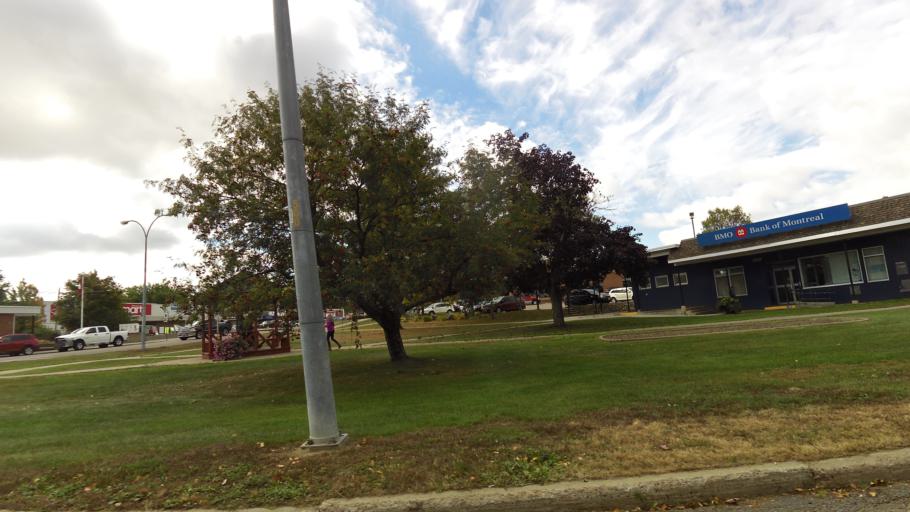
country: CA
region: Ontario
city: Deep River
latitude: 46.1016
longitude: -77.4866
